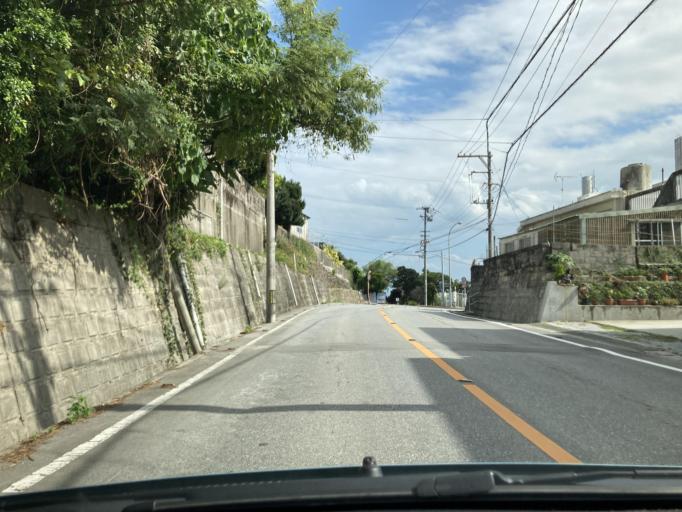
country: JP
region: Okinawa
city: Ginowan
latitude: 26.2687
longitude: 127.7855
